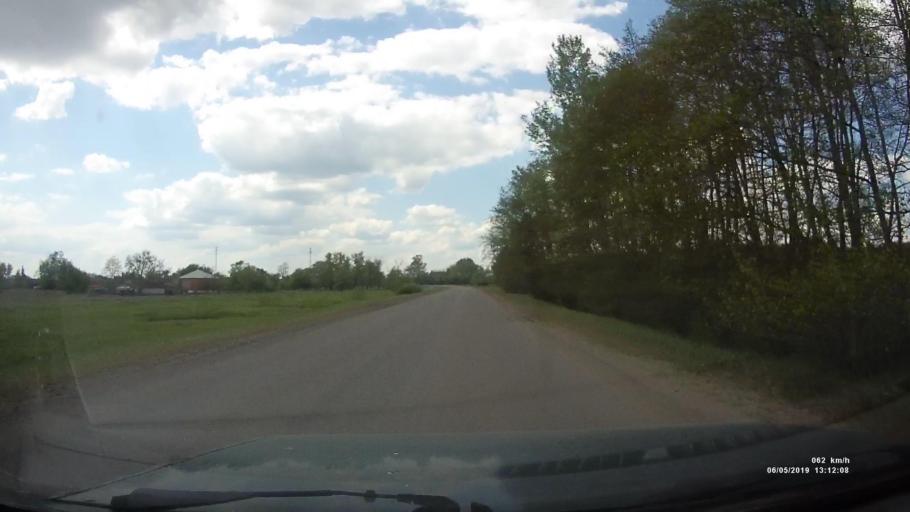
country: RU
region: Rostov
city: Ust'-Donetskiy
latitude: 47.7549
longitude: 40.9511
